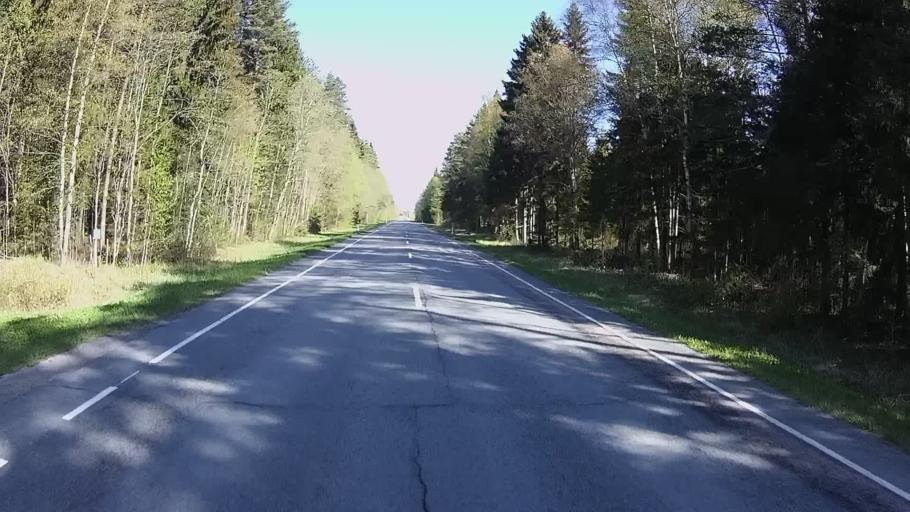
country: EE
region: Raplamaa
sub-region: Jaervakandi vald
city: Jarvakandi
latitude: 58.8267
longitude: 24.7977
